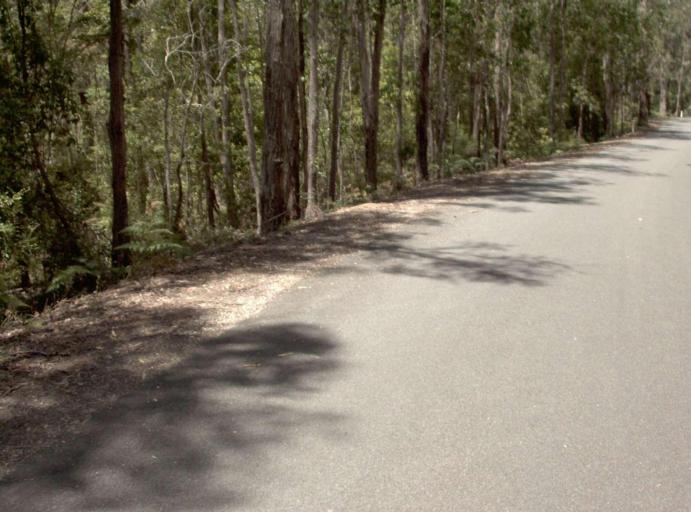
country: AU
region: New South Wales
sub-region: Bombala
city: Bombala
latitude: -37.5056
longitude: 148.9261
